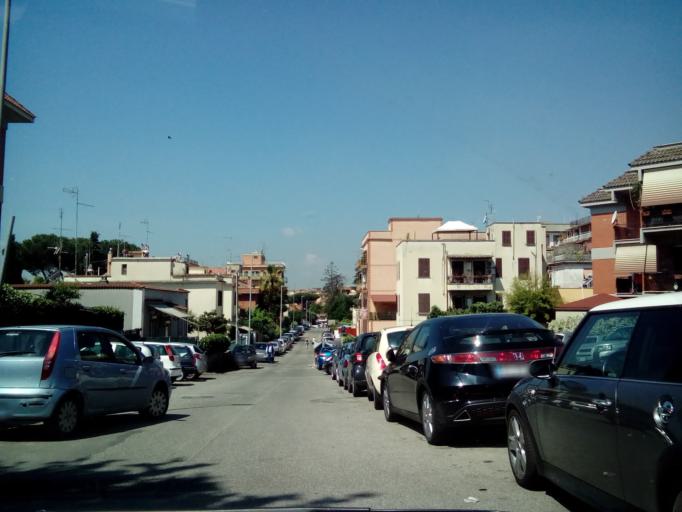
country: IT
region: Latium
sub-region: Citta metropolitana di Roma Capitale
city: Rome
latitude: 41.8799
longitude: 12.5777
